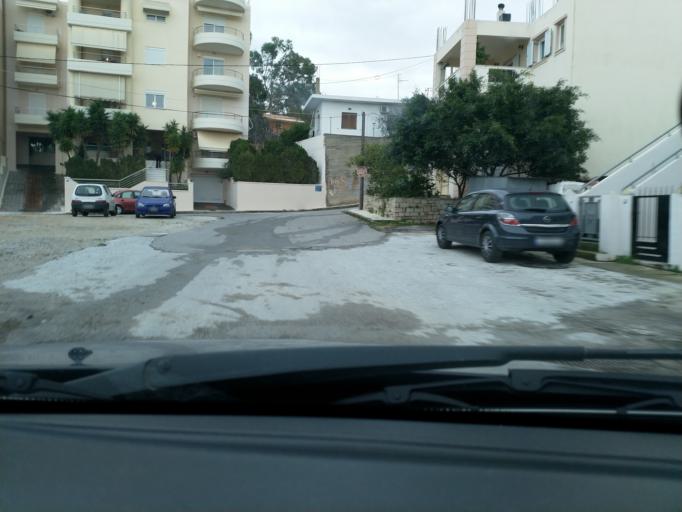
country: GR
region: Crete
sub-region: Nomos Chanias
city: Chania
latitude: 35.5112
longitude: 24.0409
